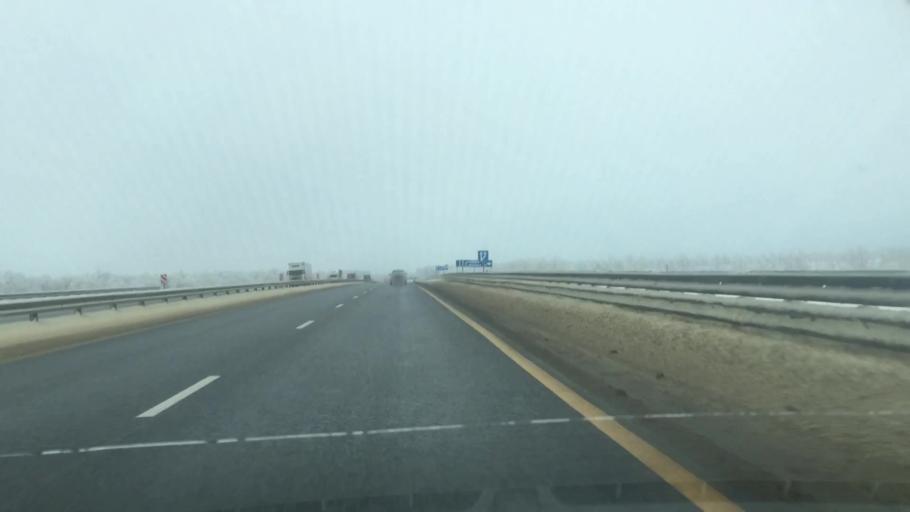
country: RU
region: Lipetsk
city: Zadonsk
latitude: 52.5043
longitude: 38.7555
